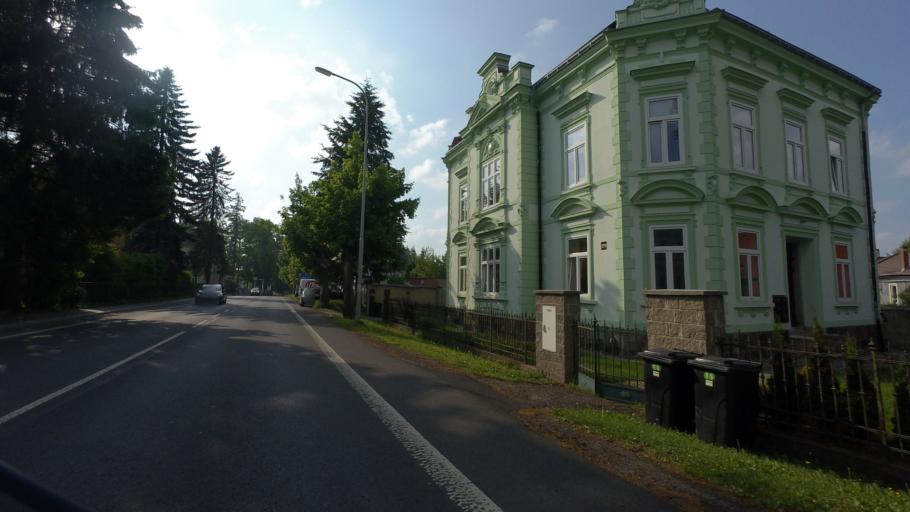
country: CZ
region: Ustecky
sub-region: Okres Decin
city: Sluknov
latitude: 51.0039
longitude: 14.4594
